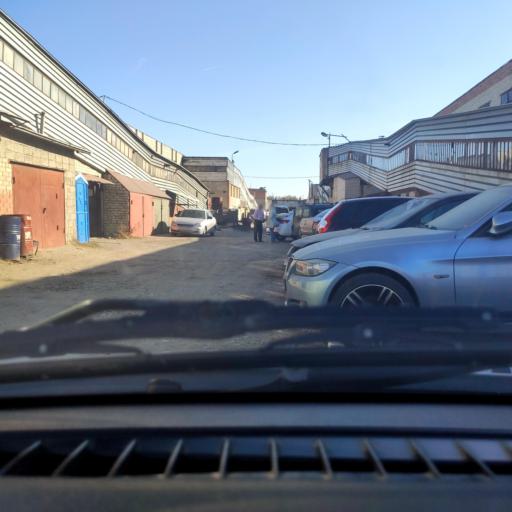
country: RU
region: Samara
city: Tol'yatti
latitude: 53.5152
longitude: 49.4317
